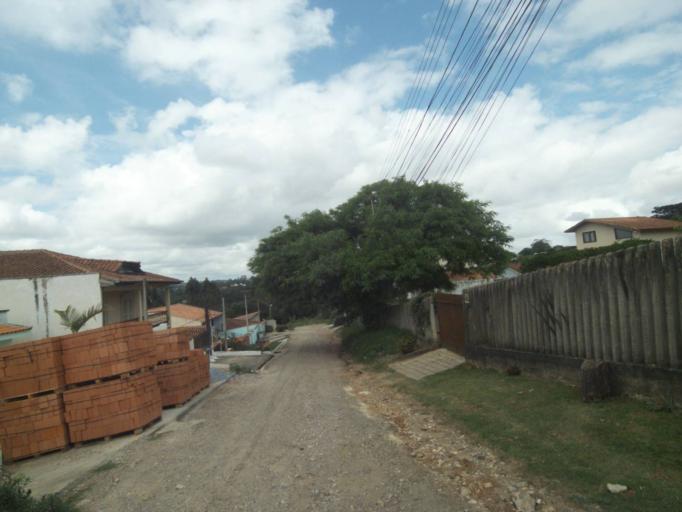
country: BR
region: Parana
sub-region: Curitiba
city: Curitiba
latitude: -25.3827
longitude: -49.2867
